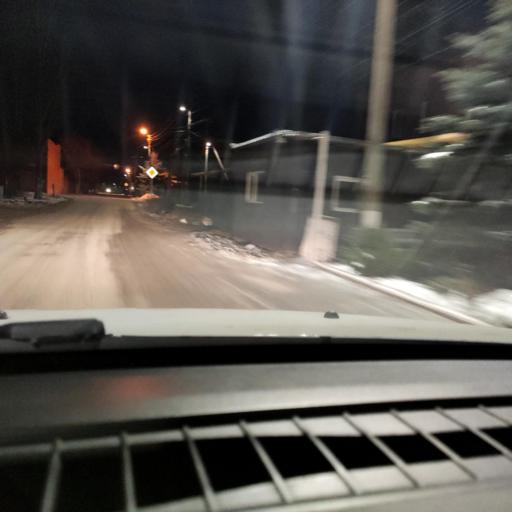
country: RU
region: Samara
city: Podstepki
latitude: 53.5170
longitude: 49.1730
